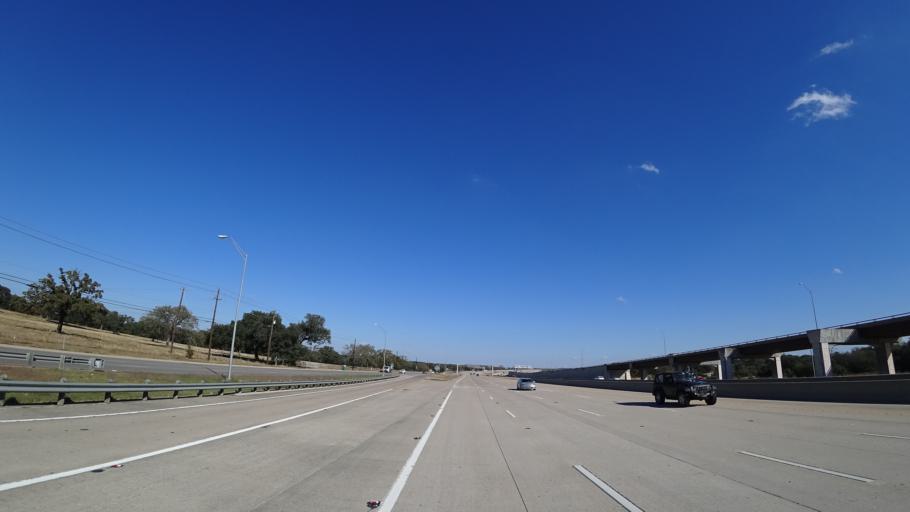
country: US
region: Texas
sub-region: Williamson County
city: Brushy Creek
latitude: 30.4794
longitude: -97.7563
